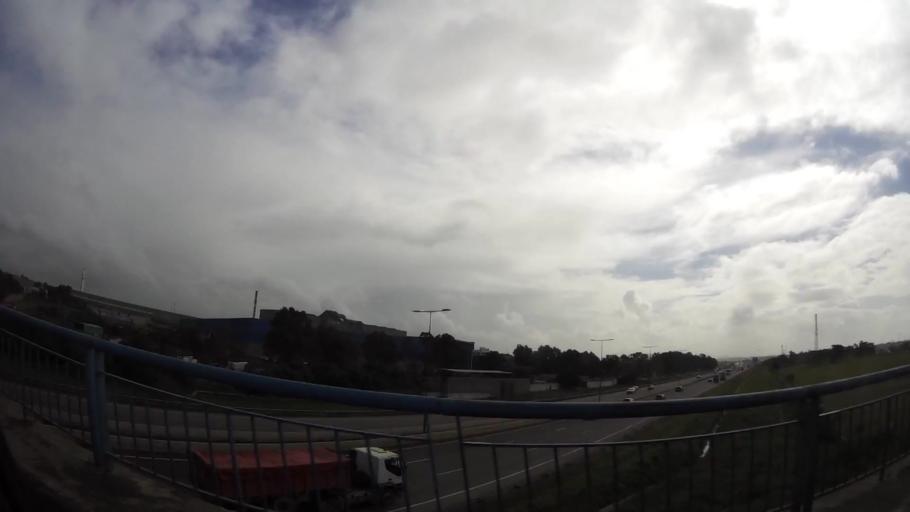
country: MA
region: Grand Casablanca
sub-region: Mohammedia
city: Mohammedia
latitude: 33.6411
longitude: -7.4351
